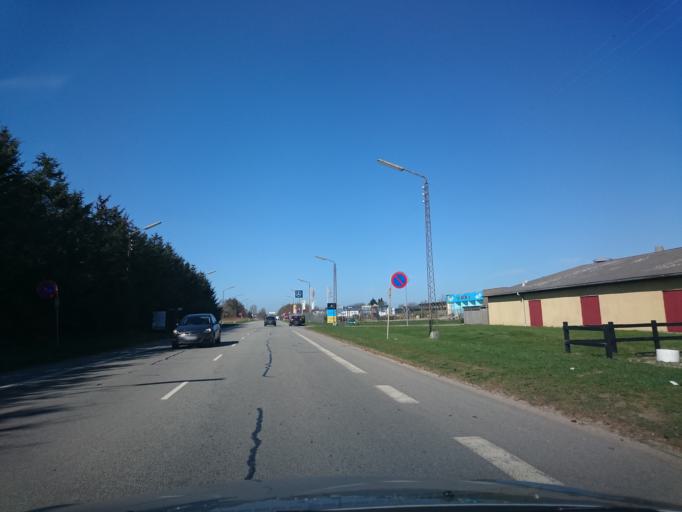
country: DK
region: North Denmark
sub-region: Hjorring Kommune
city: Hjorring
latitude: 57.4596
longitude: 10.0176
